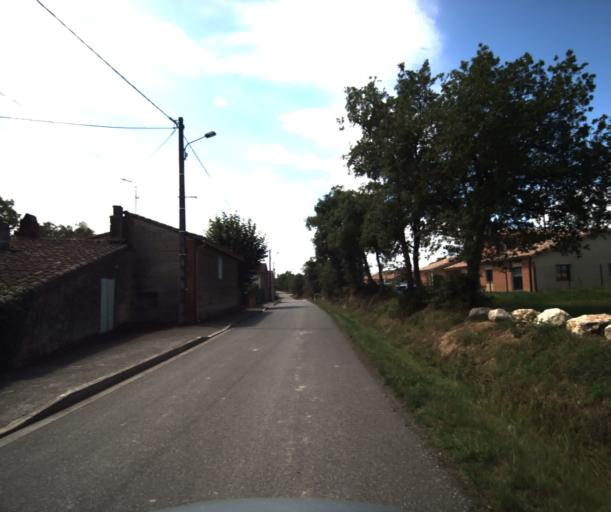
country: FR
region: Midi-Pyrenees
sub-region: Departement de la Haute-Garonne
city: Lacasse
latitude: 43.3935
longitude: 1.2653
